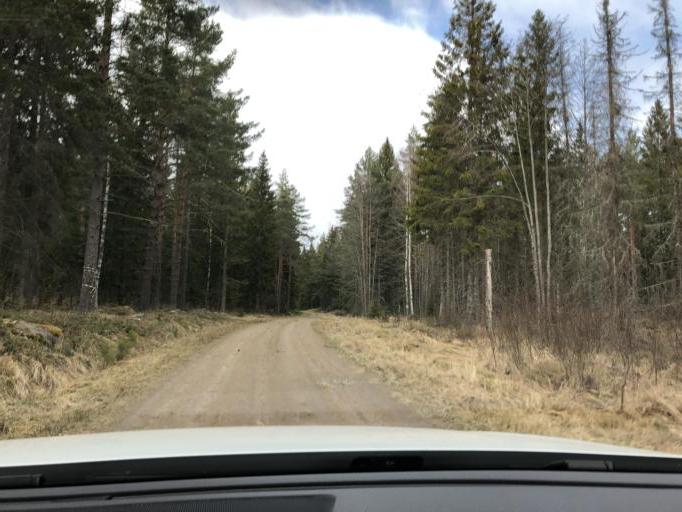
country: SE
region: Gaevleborg
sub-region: Gavle Kommun
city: Hedesunda
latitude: 60.3406
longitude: 17.1052
